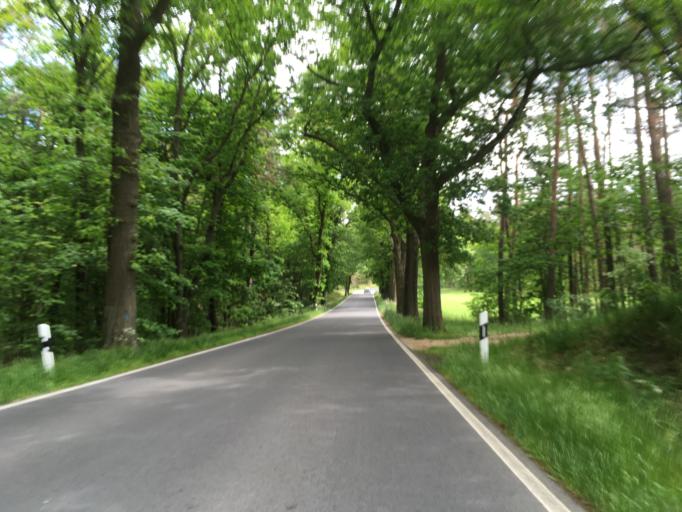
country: DE
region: Brandenburg
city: Falkenberg
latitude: 52.7649
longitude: 13.9657
